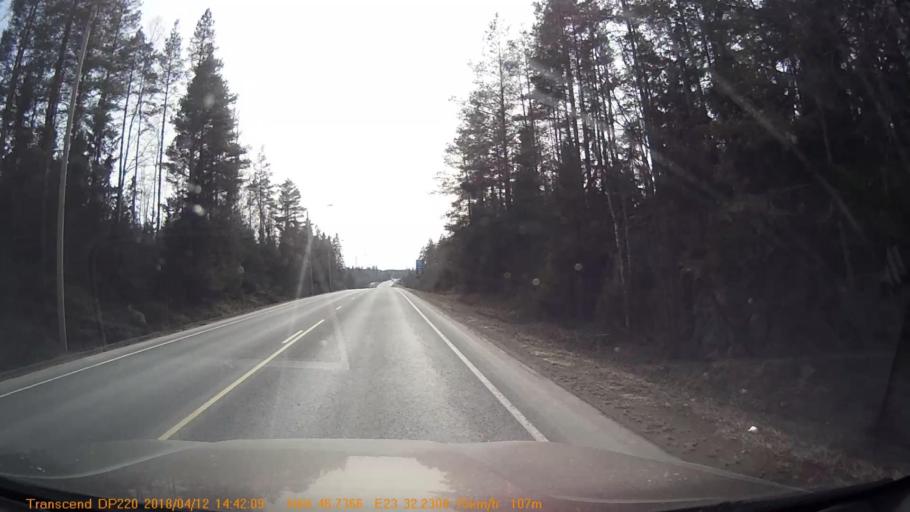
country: FI
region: Haeme
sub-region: Forssa
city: Jokioinen
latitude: 60.8120
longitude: 23.5368
